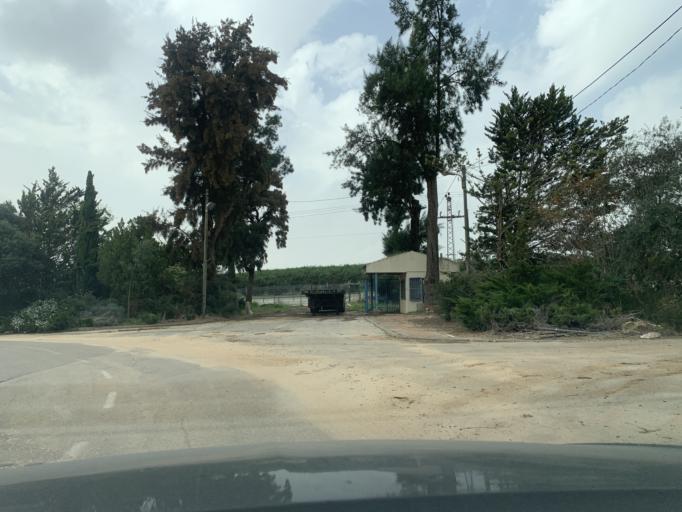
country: IL
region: Central District
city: Tirah
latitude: 32.2188
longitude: 34.9356
